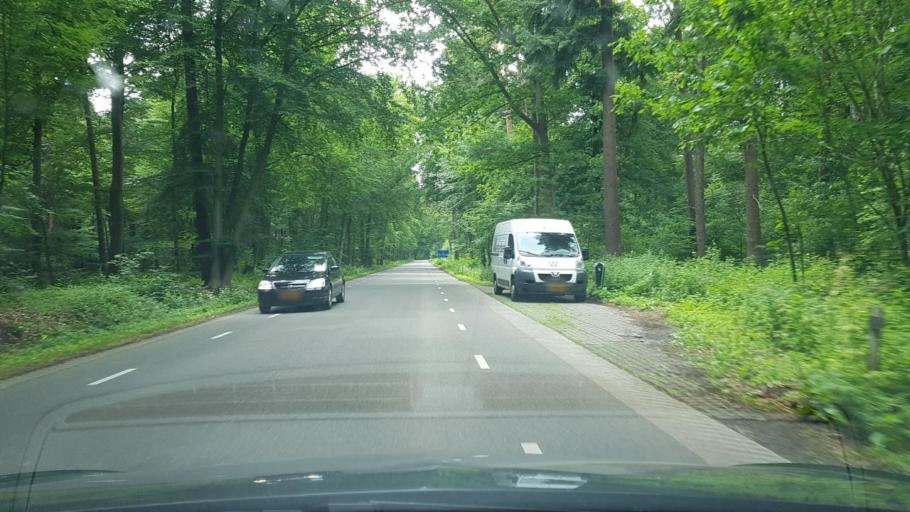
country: NL
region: Gelderland
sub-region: Gemeente Voorst
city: Voorst
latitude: 52.1891
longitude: 6.1138
